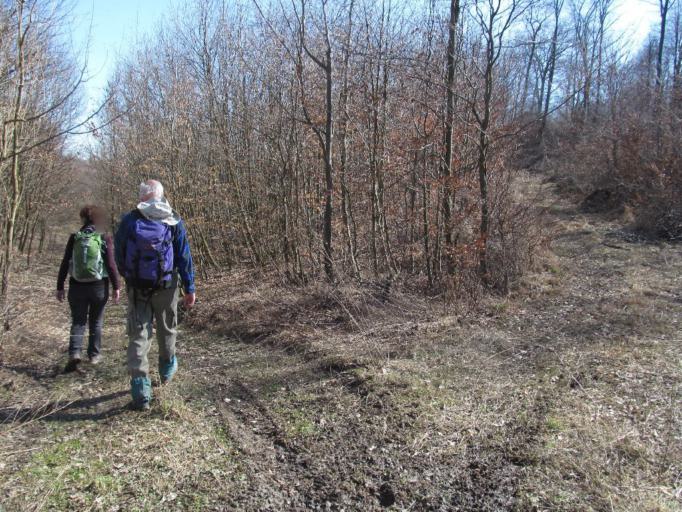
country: HU
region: Fejer
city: Bakonycsernye
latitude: 47.2721
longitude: 18.1099
